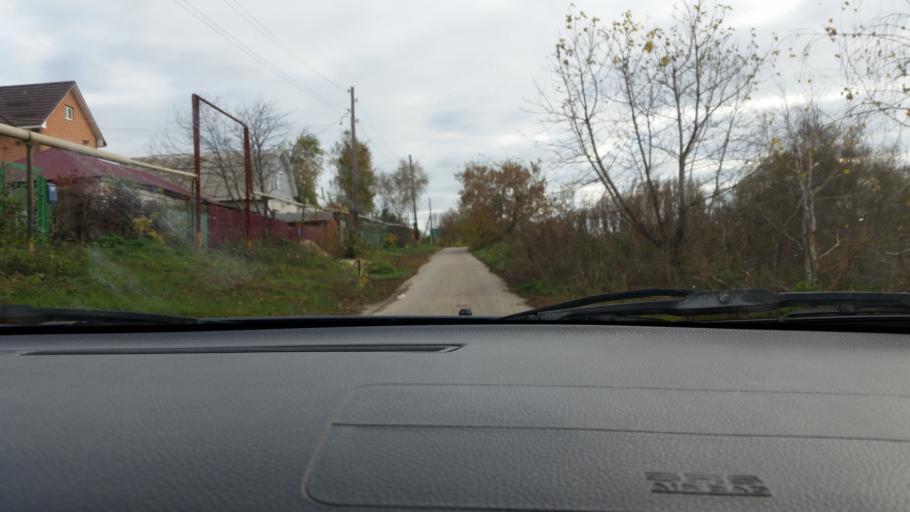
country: RU
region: Lipetsk
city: Gryazi
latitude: 52.4518
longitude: 39.9836
